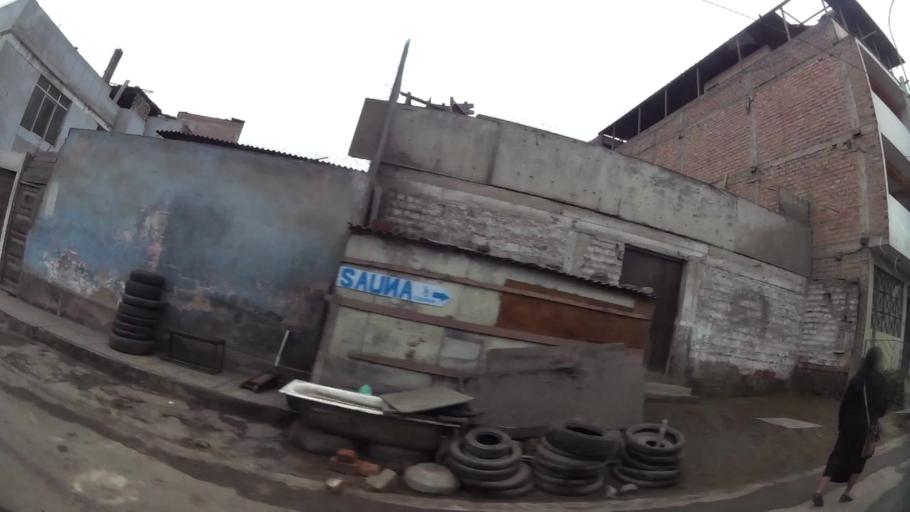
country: PE
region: Lima
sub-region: Lima
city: Surco
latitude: -12.1555
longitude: -76.9606
